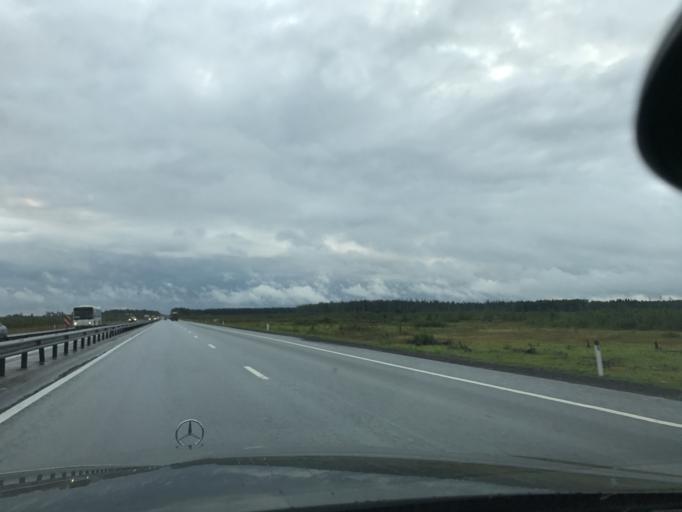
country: RU
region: Moskovskaya
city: Elektrogorsk
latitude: 55.8514
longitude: 38.8203
